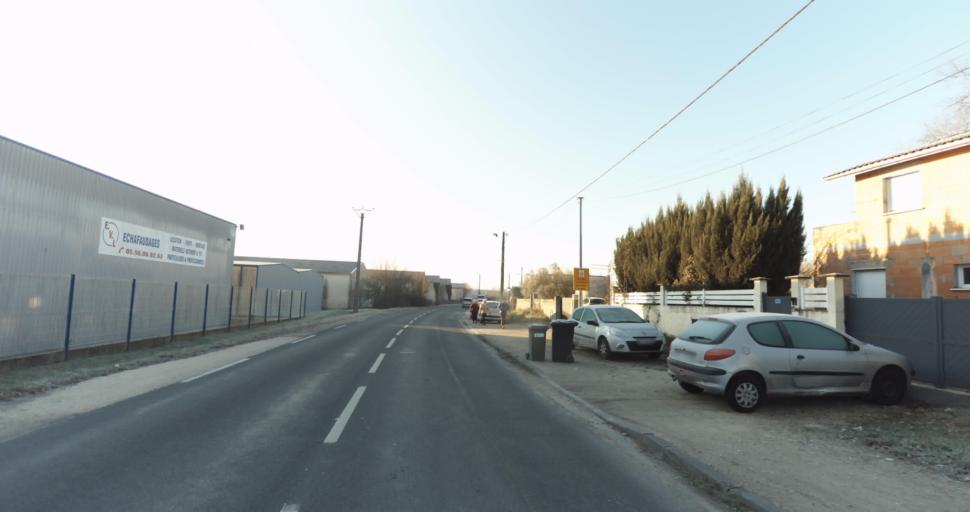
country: FR
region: Aquitaine
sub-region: Departement de la Gironde
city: Ambares-et-Lagrave
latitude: 44.9162
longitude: -0.4930
